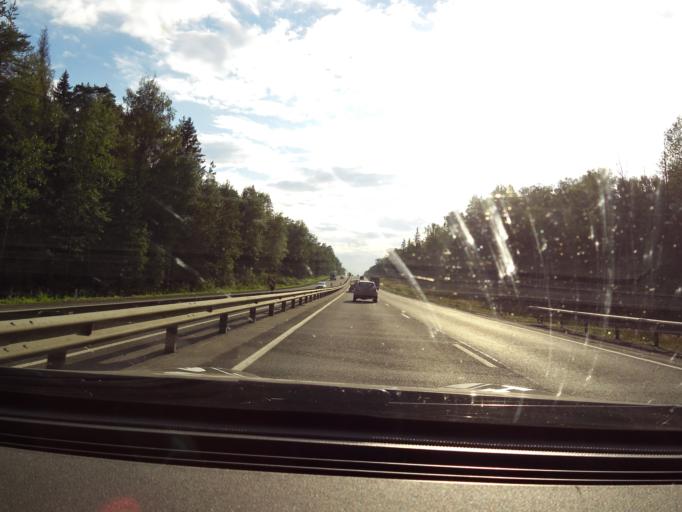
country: RU
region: Vladimir
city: Kameshkovo
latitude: 56.2004
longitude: 41.0673
